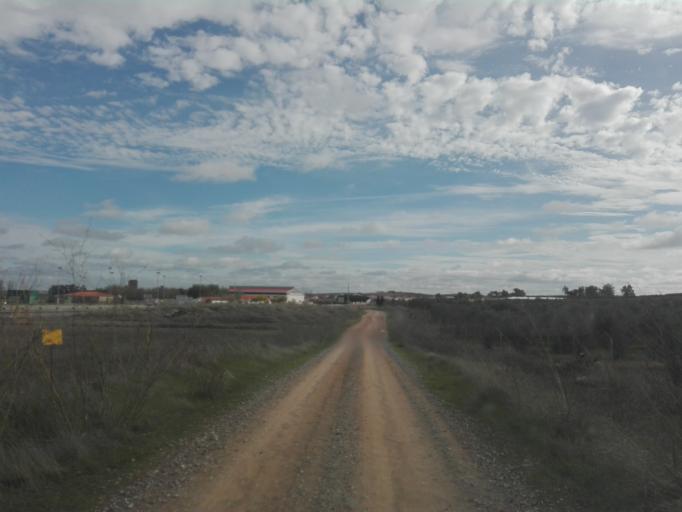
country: ES
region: Extremadura
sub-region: Provincia de Badajoz
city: Villagarcia de la Torre
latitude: 38.2926
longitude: -6.0894
